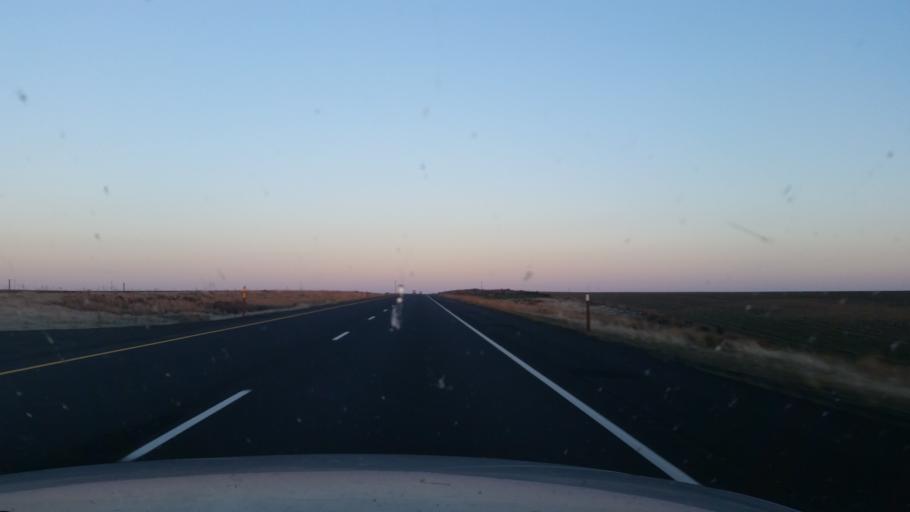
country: US
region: Washington
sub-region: Grant County
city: Warden
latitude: 47.0858
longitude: -118.8210
